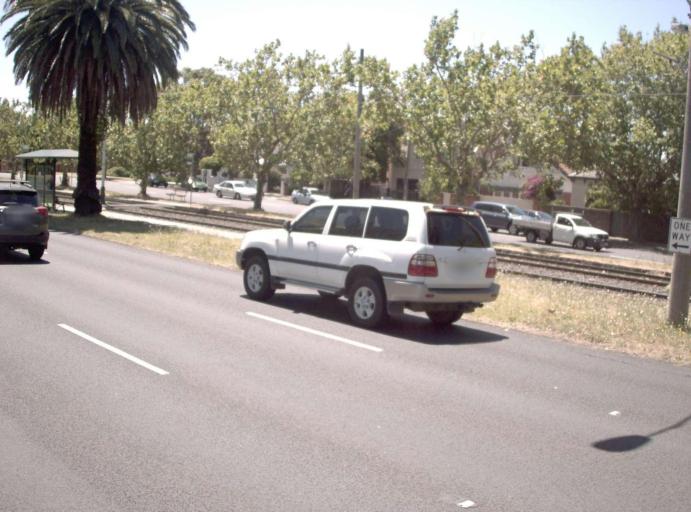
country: AU
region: Victoria
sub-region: Glen Eira
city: Caulfield North
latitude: -37.8623
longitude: 145.0180
